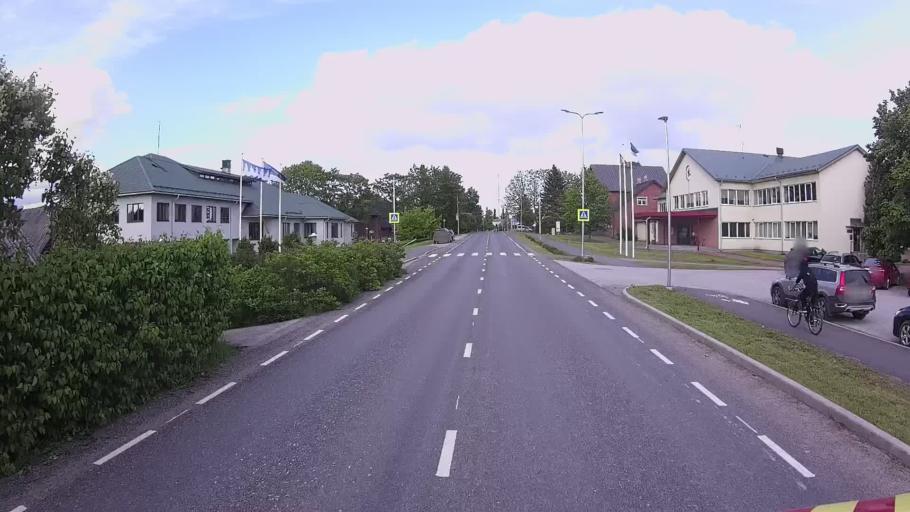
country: EE
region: Jogevamaa
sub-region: Mustvee linn
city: Mustvee
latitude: 58.9856
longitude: 26.8670
